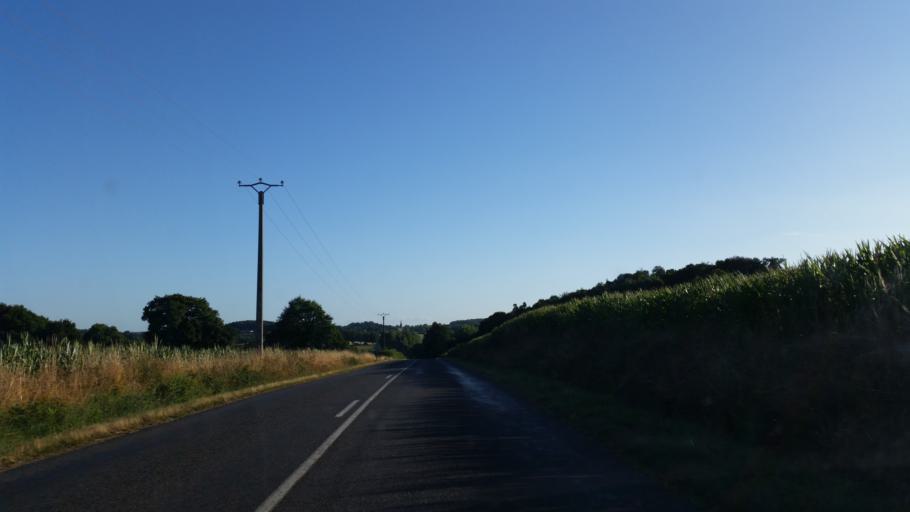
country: FR
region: Lower Normandy
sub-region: Departement du Calvados
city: Clecy
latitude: 48.8154
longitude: -0.4170
